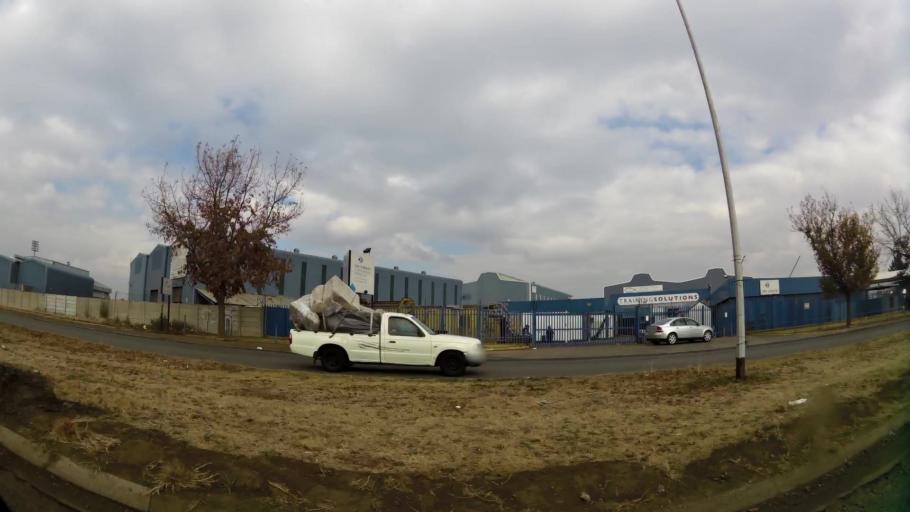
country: ZA
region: Gauteng
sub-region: Sedibeng District Municipality
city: Vanderbijlpark
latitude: -26.7009
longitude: 27.8588
